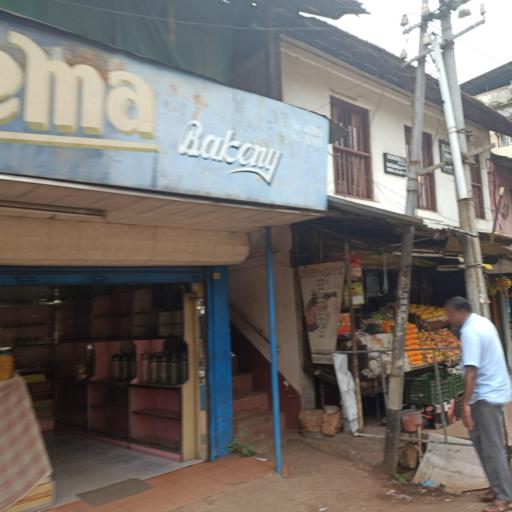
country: IN
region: Kerala
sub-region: Kasaragod District
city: Kasaragod
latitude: 12.5016
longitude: 74.9872
